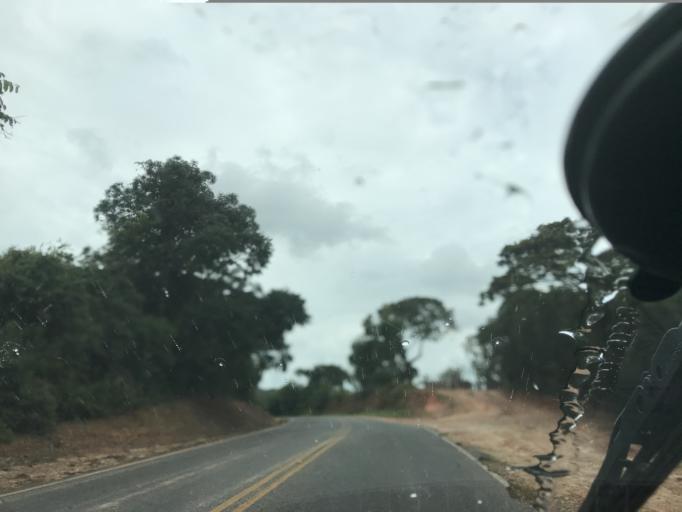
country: BR
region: Minas Gerais
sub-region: Conceicao Do Rio Verde
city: Conceicao do Rio Verde
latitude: -21.6774
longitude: -45.0188
